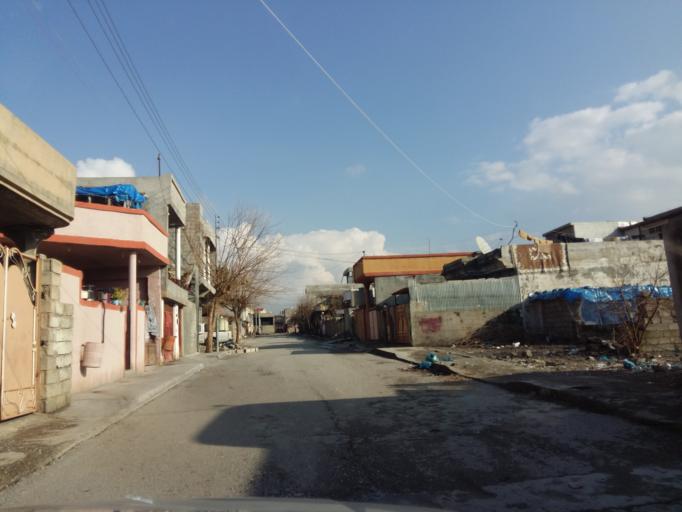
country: IQ
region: As Sulaymaniyah
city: Qeladize
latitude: 36.1769
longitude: 45.1386
